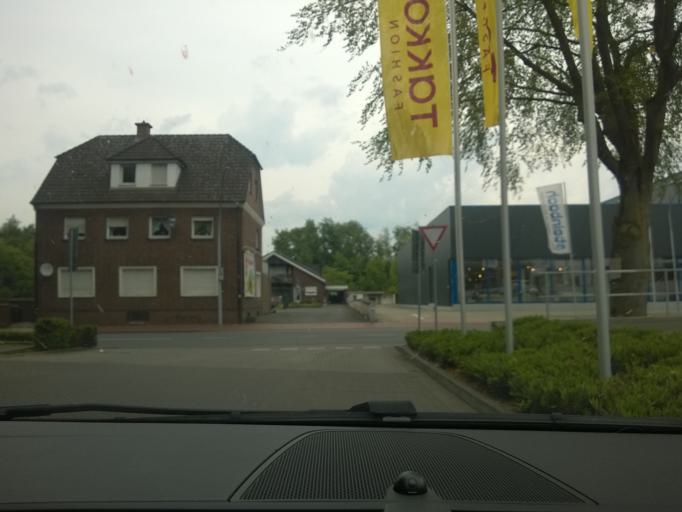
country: DE
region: North Rhine-Westphalia
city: Stadtlohn
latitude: 51.9942
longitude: 6.9181
